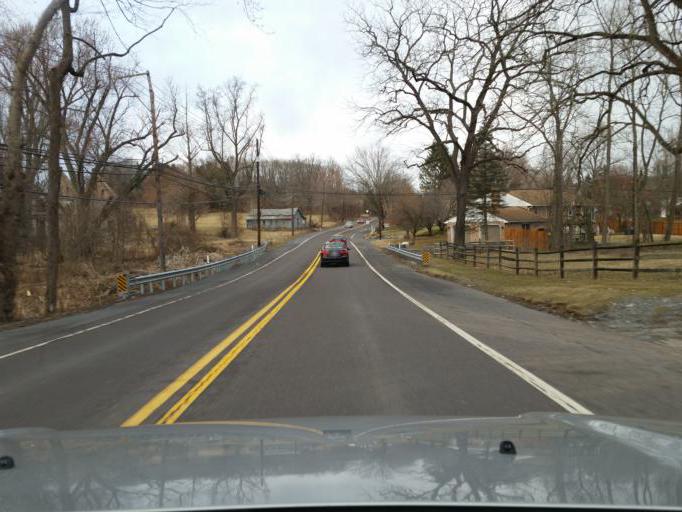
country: US
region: Pennsylvania
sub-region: Dauphin County
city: Hummelstown
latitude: 40.2328
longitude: -76.7166
